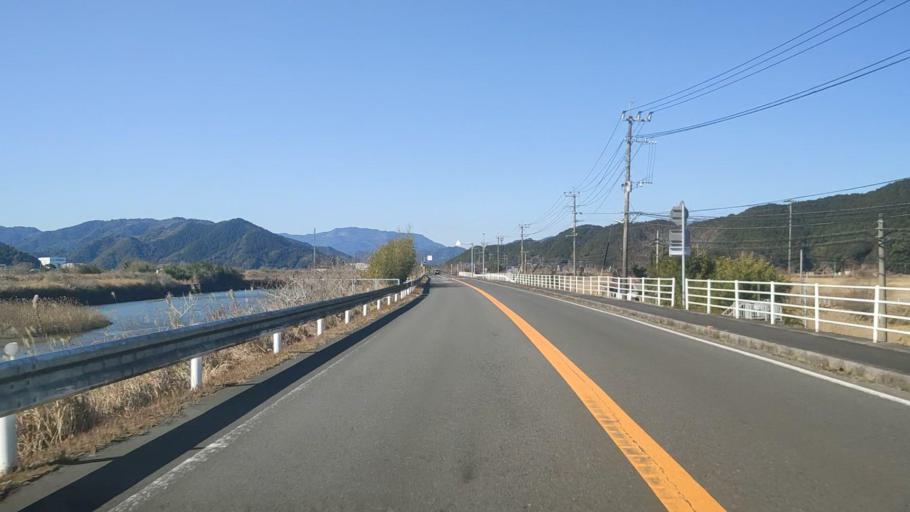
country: JP
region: Oita
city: Saiki
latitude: 32.9352
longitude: 131.9204
